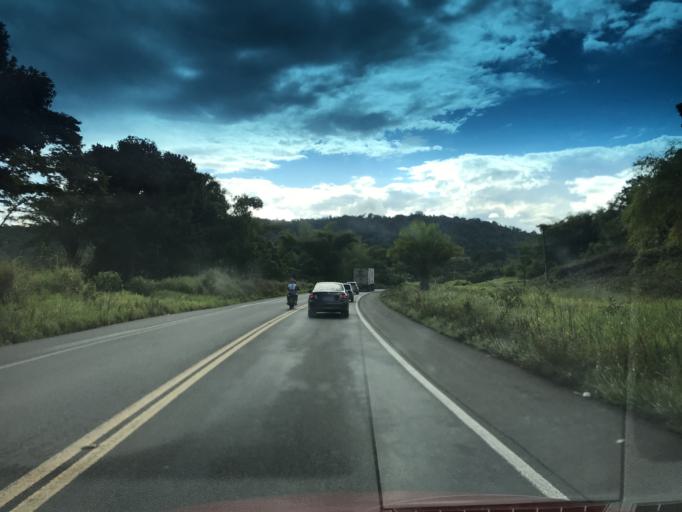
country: BR
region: Bahia
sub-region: Ibirapitanga
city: Ibirapitanga
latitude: -14.1711
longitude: -39.3254
